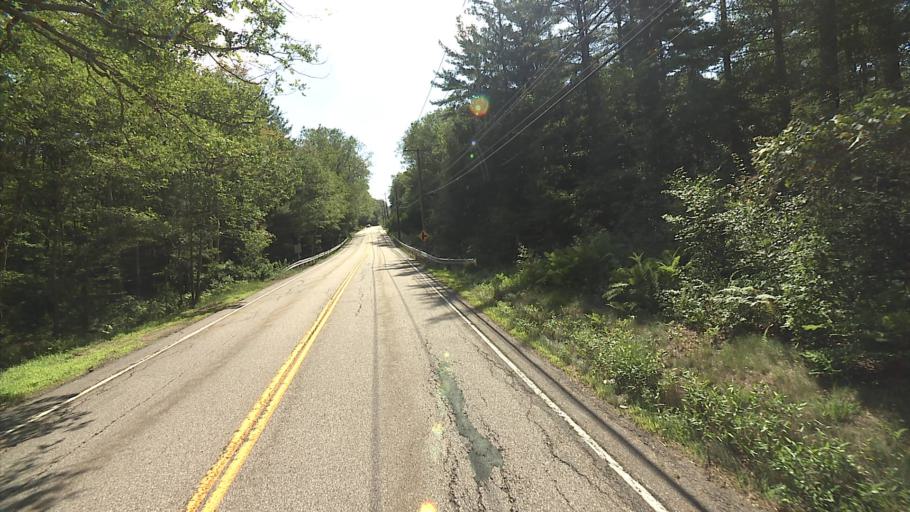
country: US
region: Connecticut
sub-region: Tolland County
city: Stafford
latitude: 41.9637
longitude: -72.2239
